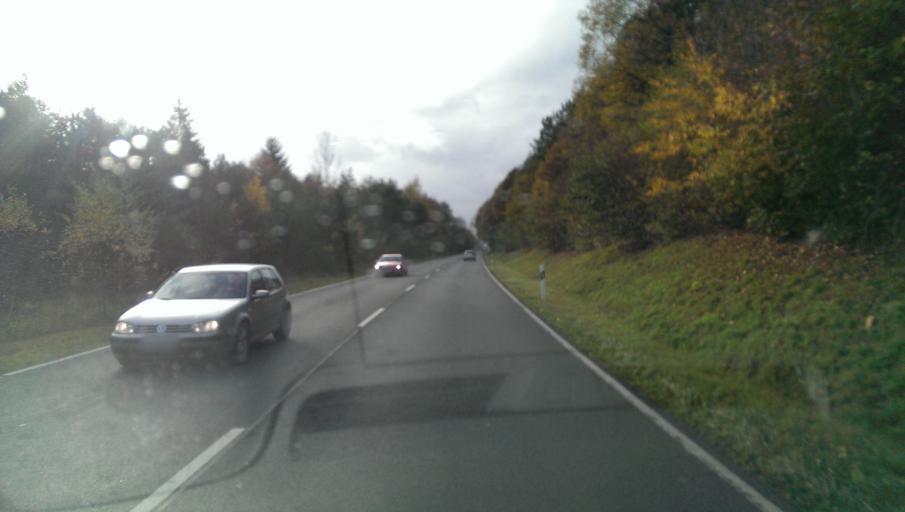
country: DE
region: Baden-Wuerttemberg
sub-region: Karlsruhe Region
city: Buchen
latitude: 49.5043
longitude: 9.2960
